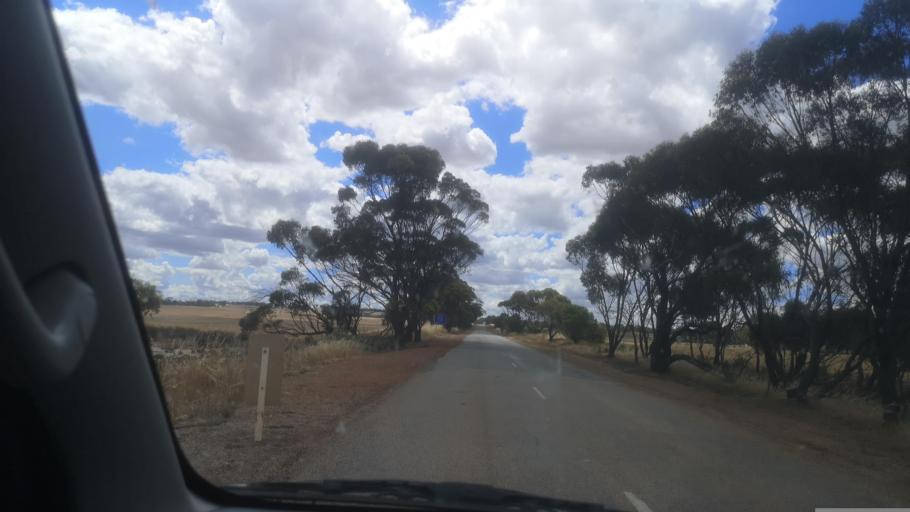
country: AU
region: Western Australia
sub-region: Beverley
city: Beverley
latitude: -31.9788
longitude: 117.0851
